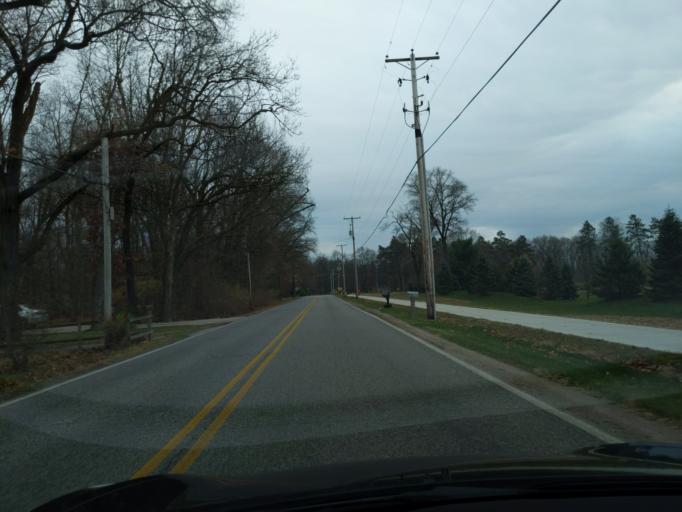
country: US
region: Indiana
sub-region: Saint Joseph County
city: Georgetown
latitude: 41.7330
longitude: -86.2653
